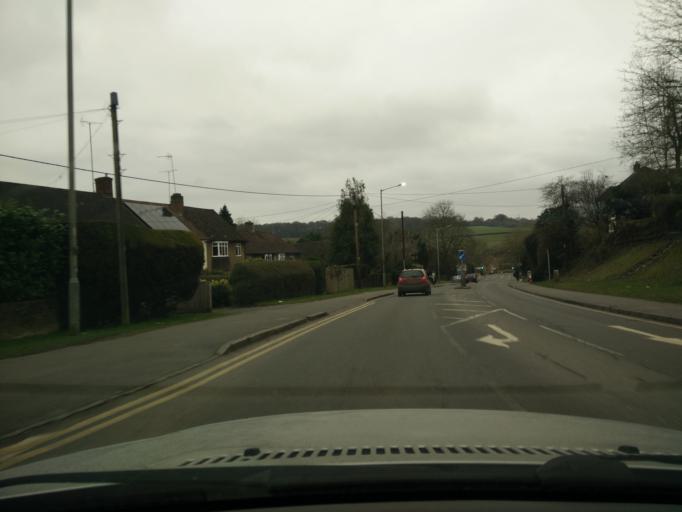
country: GB
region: England
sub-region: Buckinghamshire
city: Amersham on the Hill
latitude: 51.6672
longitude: -0.6068
